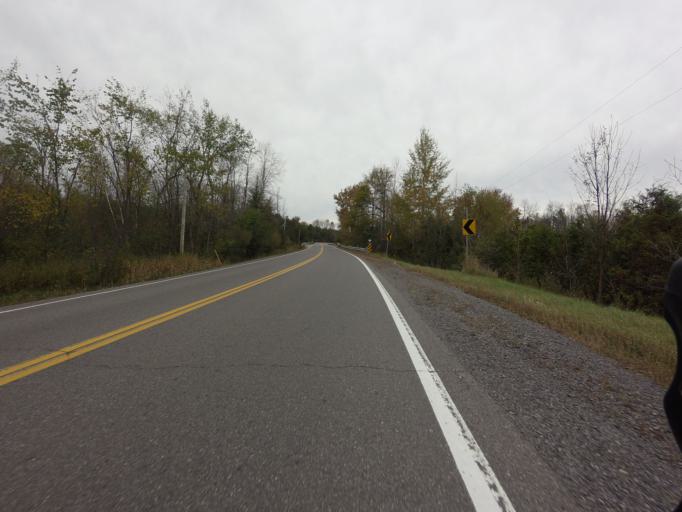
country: CA
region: Ontario
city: Brockville
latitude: 44.8048
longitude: -75.7951
